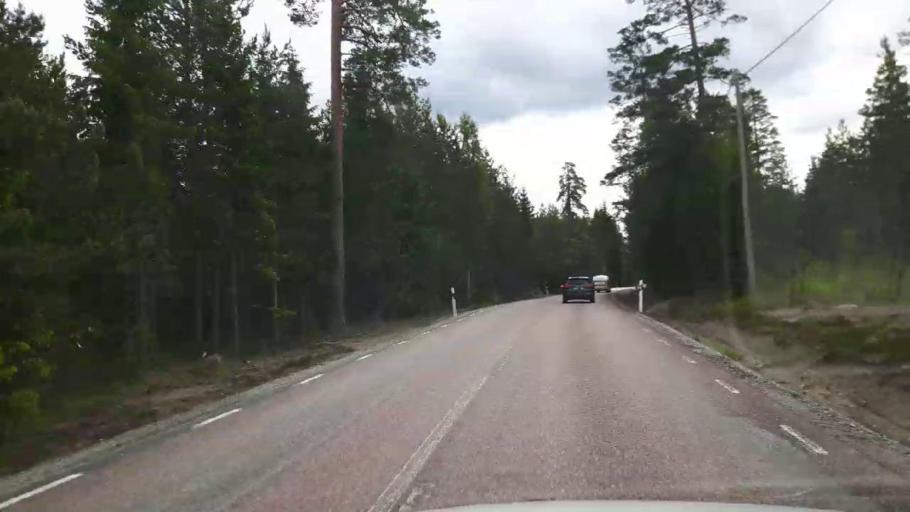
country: SE
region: Vaestmanland
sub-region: Skinnskattebergs Kommun
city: Skinnskatteberg
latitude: 59.8158
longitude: 15.8394
